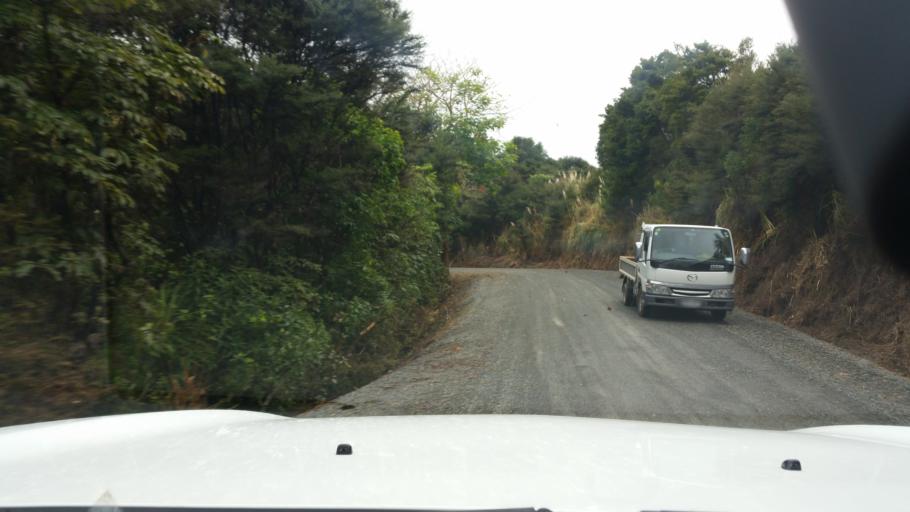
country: NZ
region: Northland
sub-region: Whangarei
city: Whangarei
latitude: -35.7336
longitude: 174.4389
